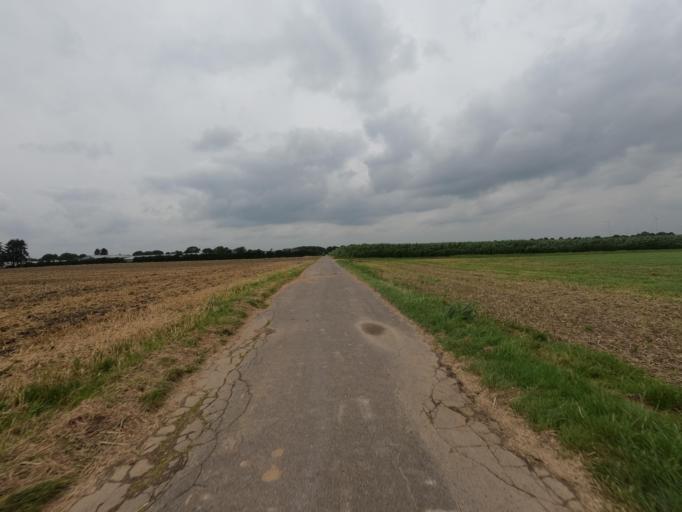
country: DE
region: North Rhine-Westphalia
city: Baesweiler
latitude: 50.9594
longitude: 6.1726
